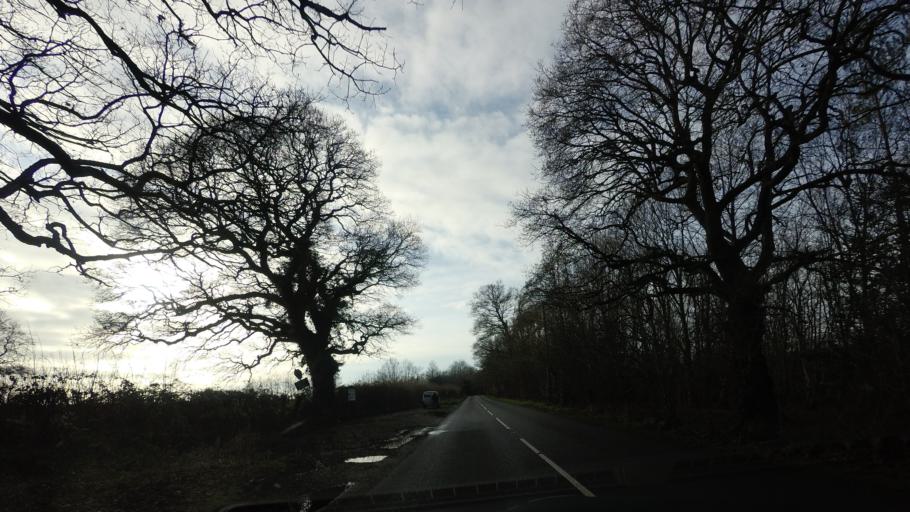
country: GB
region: England
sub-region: East Sussex
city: Battle
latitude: 50.9068
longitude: 0.4822
